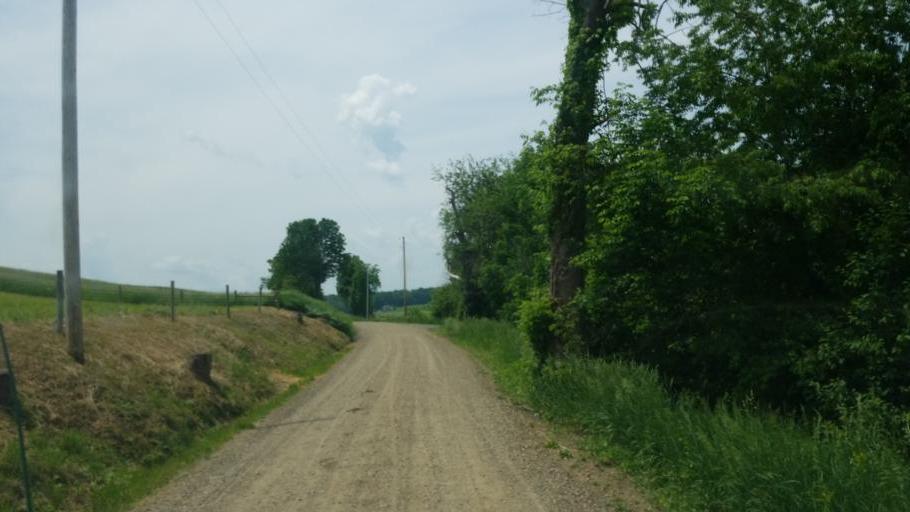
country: US
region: Ohio
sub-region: Tuscarawas County
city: Sugarcreek
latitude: 40.4735
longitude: -81.7592
